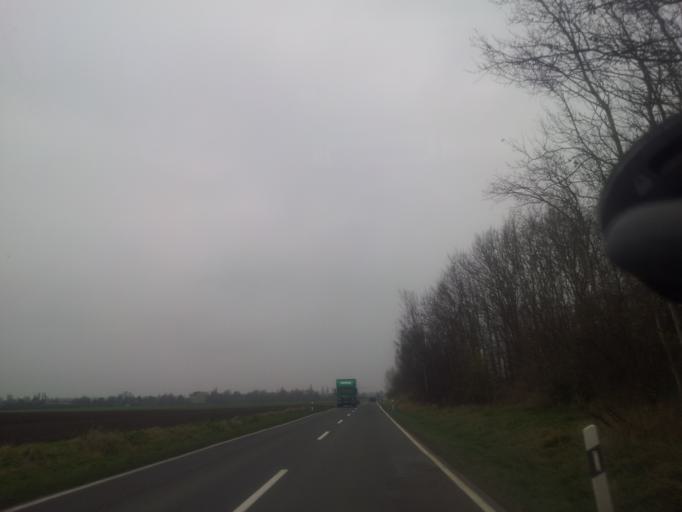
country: DE
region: Saxony-Anhalt
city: Oppin
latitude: 51.5368
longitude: 12.0101
